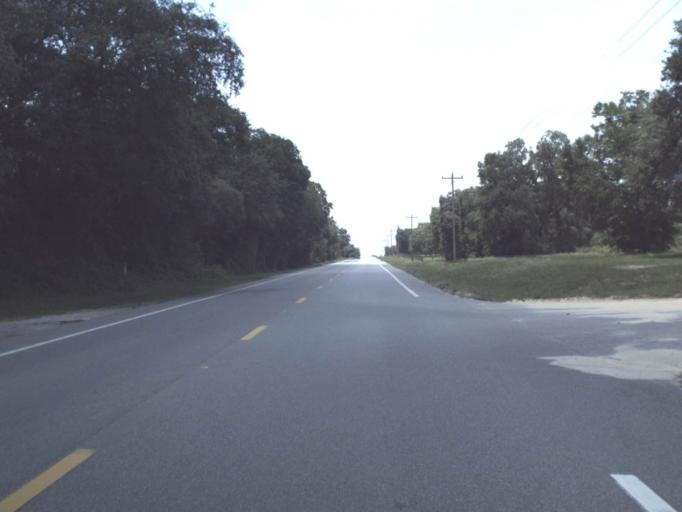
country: US
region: Florida
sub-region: Clay County
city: Keystone Heights
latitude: 29.7415
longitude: -81.9712
